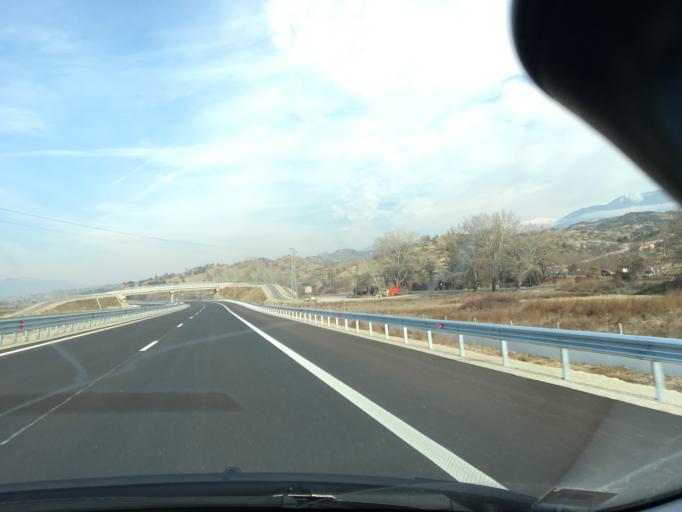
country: BG
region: Blagoevgrad
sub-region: Obshtina Strumyani
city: Strumyani
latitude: 41.6043
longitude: 23.2244
